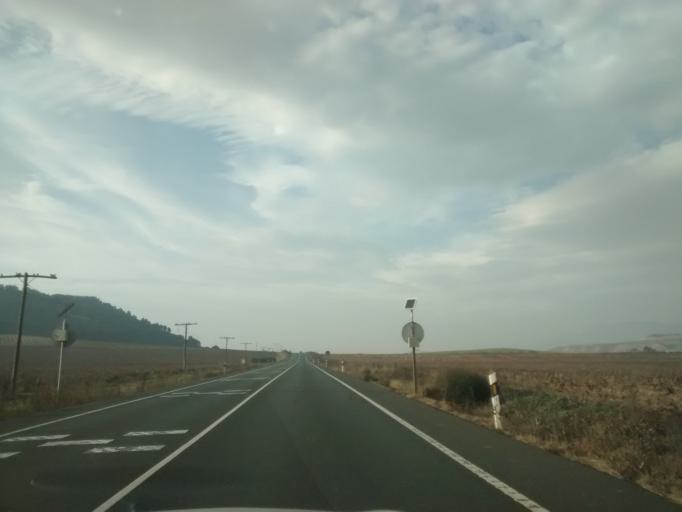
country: ES
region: La Rioja
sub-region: Provincia de La Rioja
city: Torremontalbo
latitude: 42.5026
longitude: -2.6873
